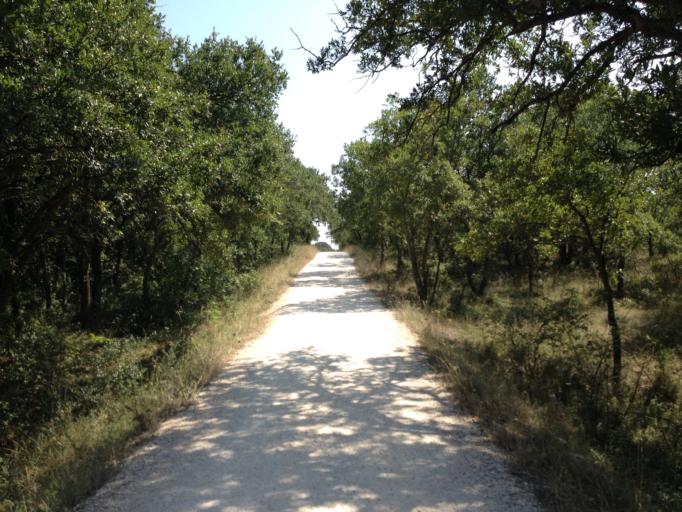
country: IT
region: Apulia
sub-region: Provincia di Brindisi
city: Cisternino
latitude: 40.7113
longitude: 17.4096
